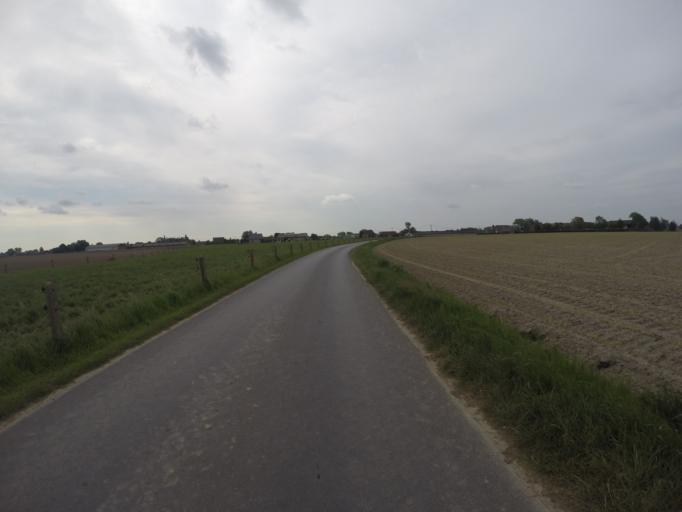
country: BE
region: Flanders
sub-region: Provincie West-Vlaanderen
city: Tielt
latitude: 51.0417
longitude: 3.3210
